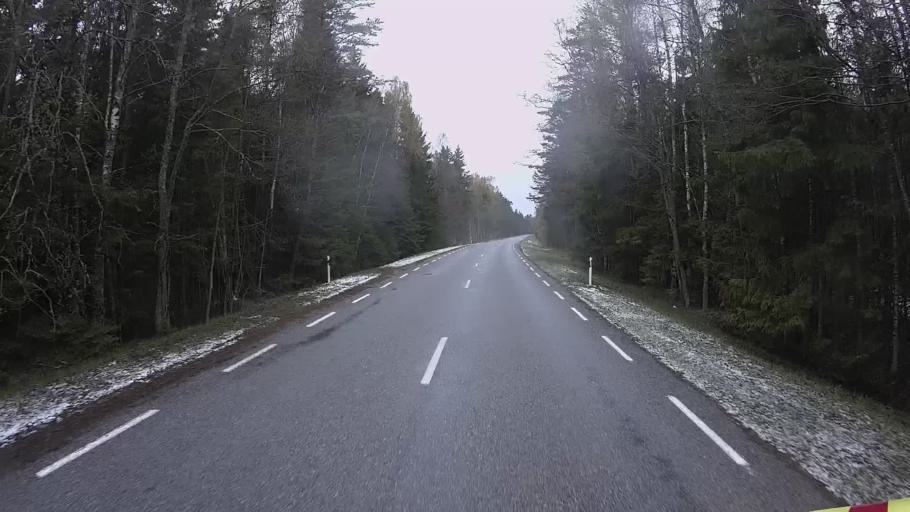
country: EE
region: Hiiumaa
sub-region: Kaerdla linn
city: Kardla
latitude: 59.0419
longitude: 22.6818
